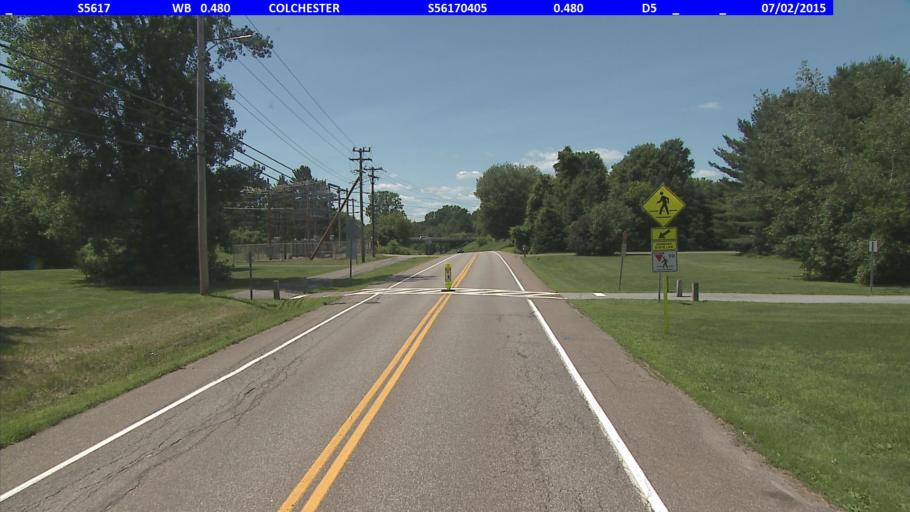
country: US
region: Vermont
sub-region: Chittenden County
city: Colchester
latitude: 44.5537
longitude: -73.1815
